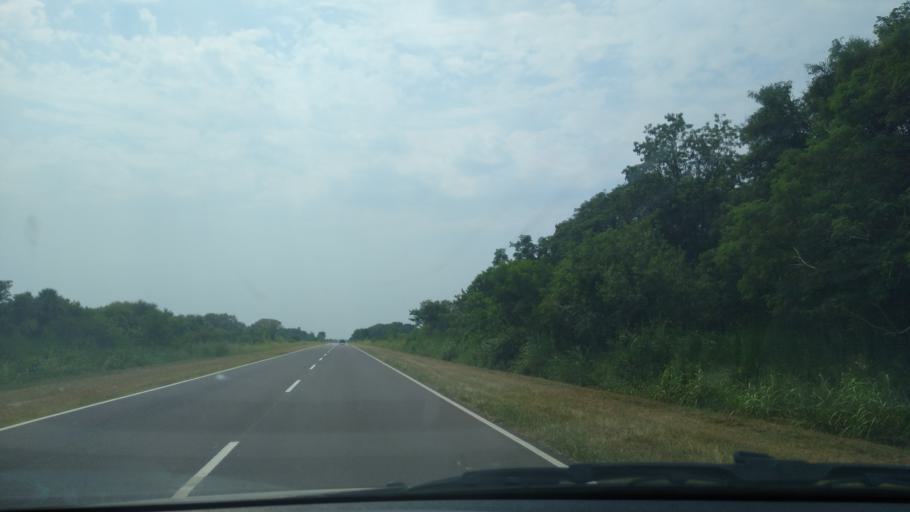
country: AR
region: Chaco
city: La Eduvigis
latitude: -27.0116
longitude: -58.9701
